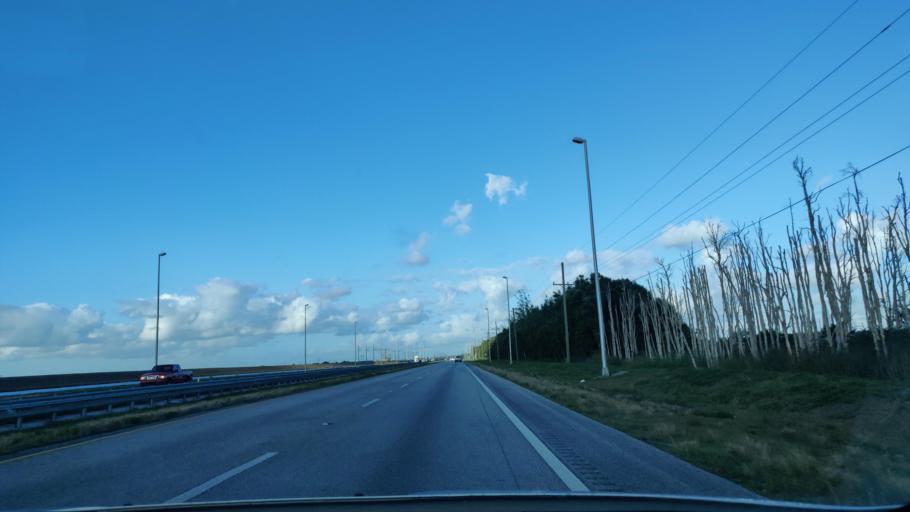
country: US
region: Florida
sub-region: Miami-Dade County
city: Palm Springs North
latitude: 25.9169
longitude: -80.4619
